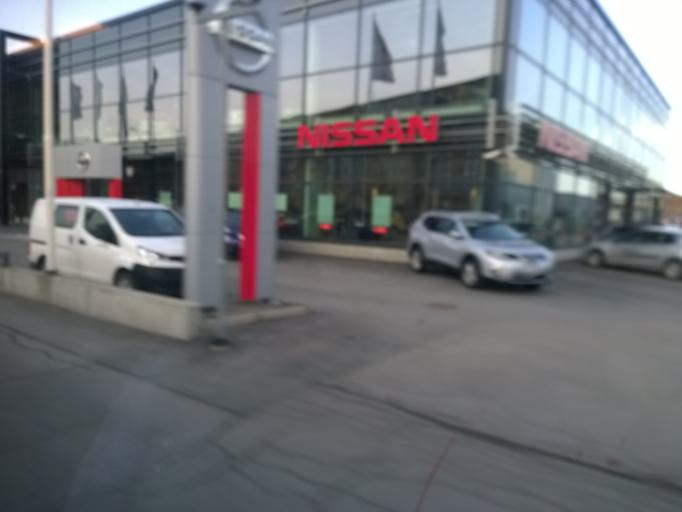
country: FI
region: Pirkanmaa
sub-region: Tampere
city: Tampere
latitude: 61.4821
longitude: 23.7634
